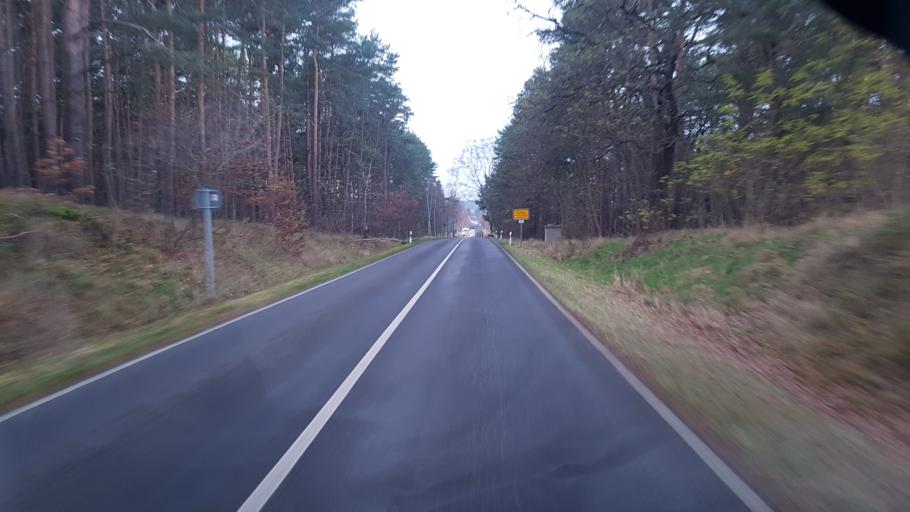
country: DE
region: Brandenburg
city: Gross Lindow
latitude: 52.1857
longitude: 14.5425
